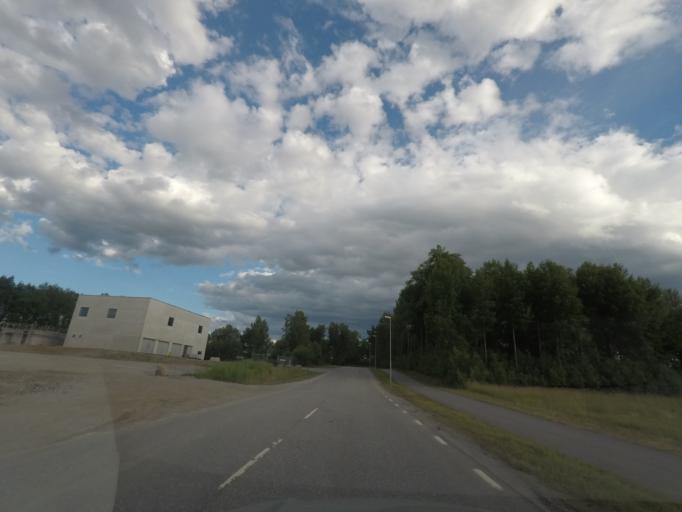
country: SE
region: Stockholm
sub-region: Sigtuna Kommun
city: Marsta
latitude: 59.6350
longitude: 17.9034
